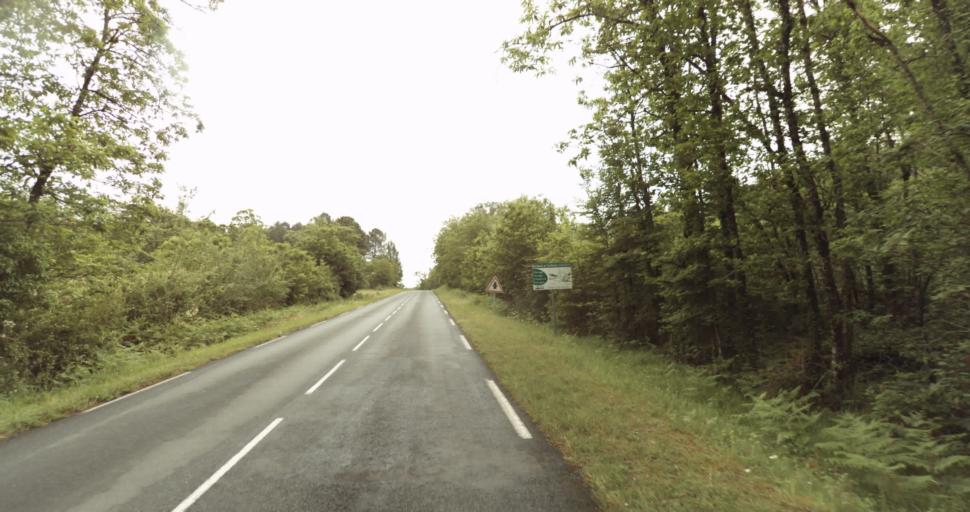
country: FR
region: Aquitaine
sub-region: Departement de la Dordogne
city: Belves
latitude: 44.6726
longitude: 0.9982
